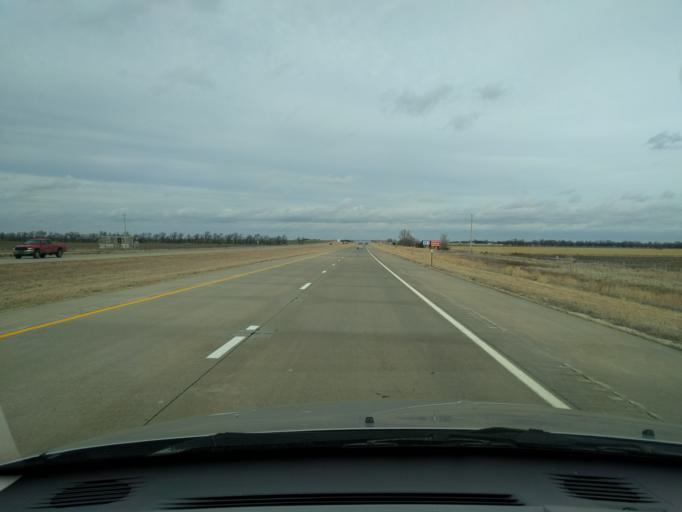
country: US
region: Kansas
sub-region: McPherson County
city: Lindsborg
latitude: 38.6953
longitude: -97.6215
